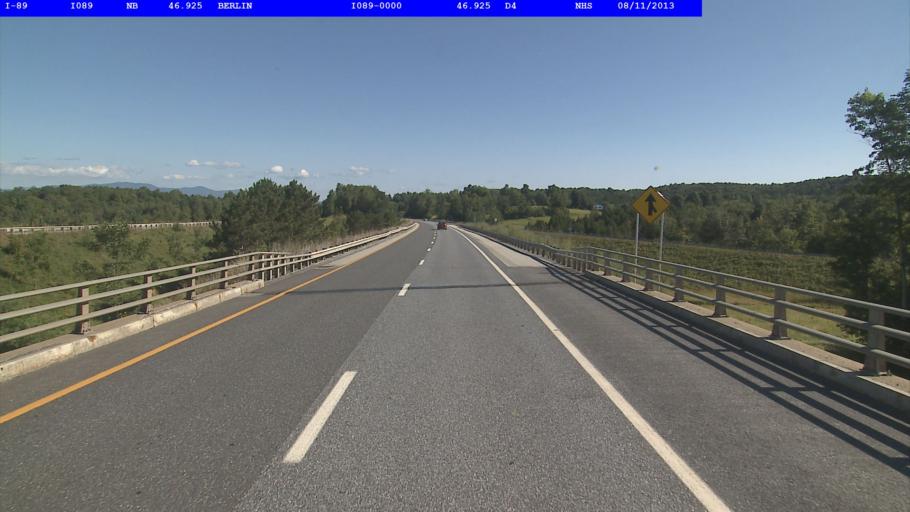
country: US
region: Vermont
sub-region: Orange County
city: Williamstown
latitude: 44.1679
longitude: -72.5772
